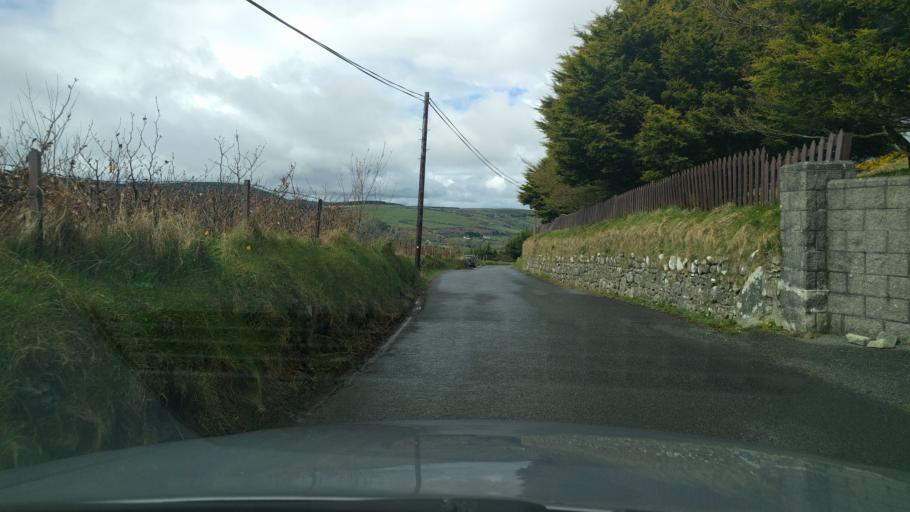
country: IE
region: Leinster
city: Oldbawn
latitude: 53.2372
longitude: -6.3503
